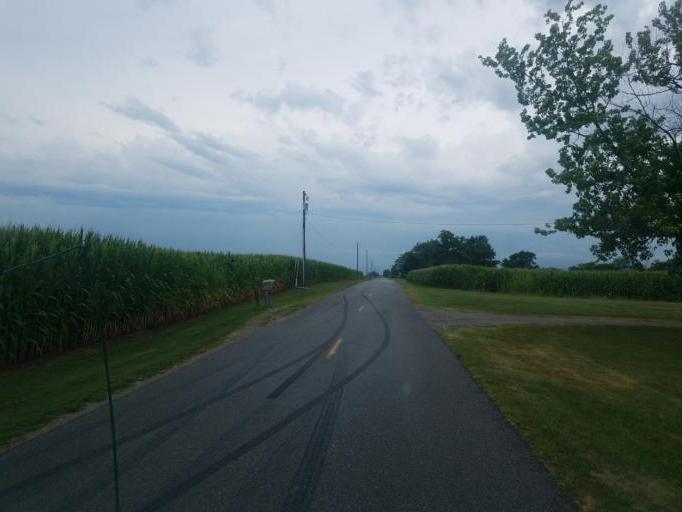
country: US
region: Ohio
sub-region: Paulding County
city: Antwerp
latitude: 41.2374
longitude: -84.7256
